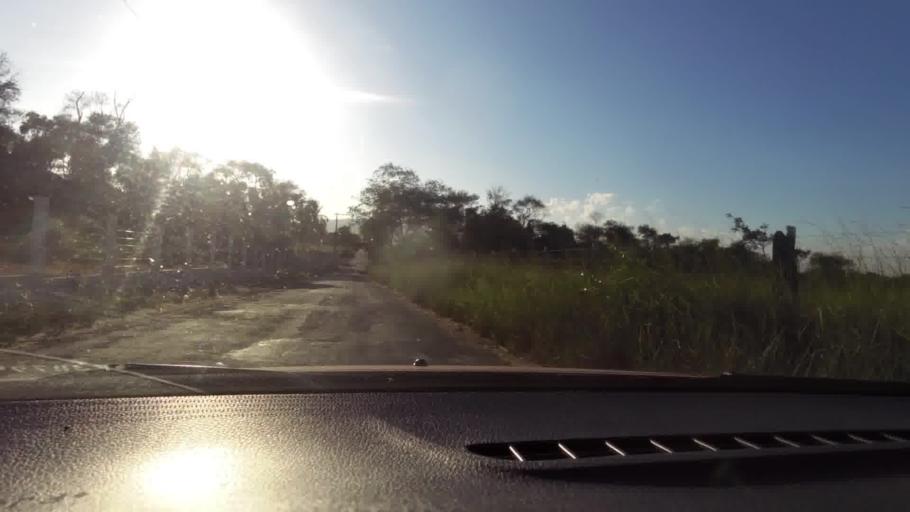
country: BR
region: Espirito Santo
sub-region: Guarapari
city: Guarapari
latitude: -20.5332
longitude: -40.4557
